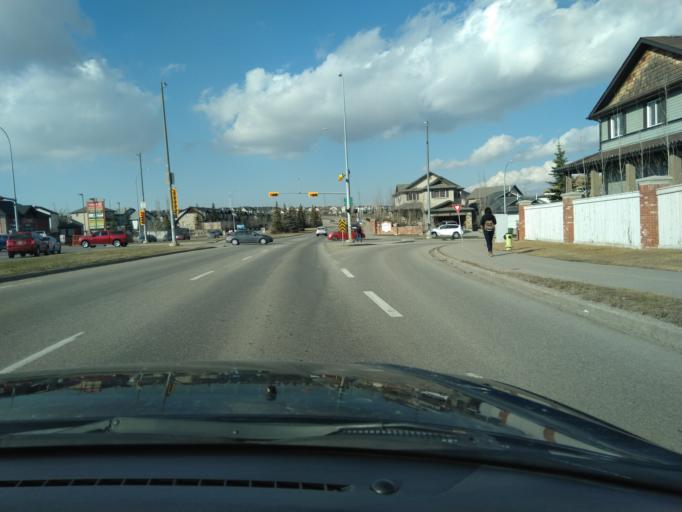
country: CA
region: Alberta
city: Calgary
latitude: 51.1638
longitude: -114.0705
